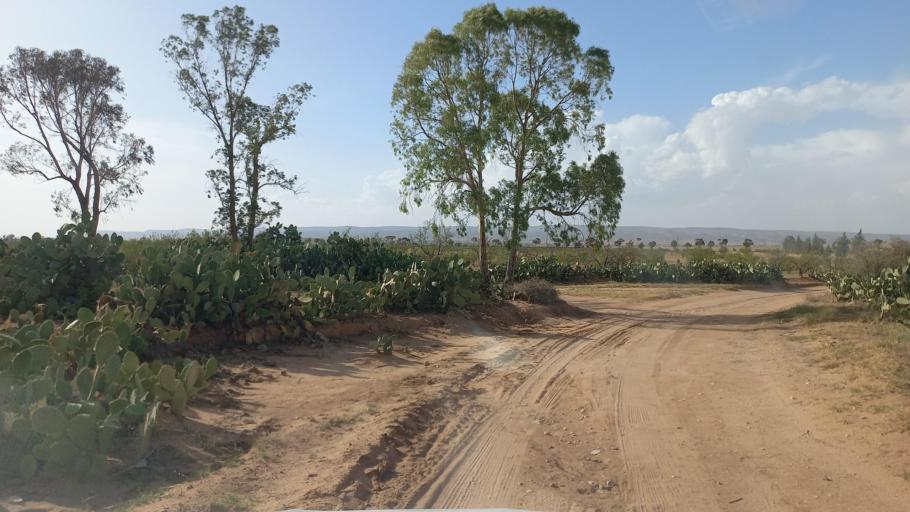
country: TN
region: Al Qasrayn
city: Kasserine
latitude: 35.2266
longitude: 8.9680
